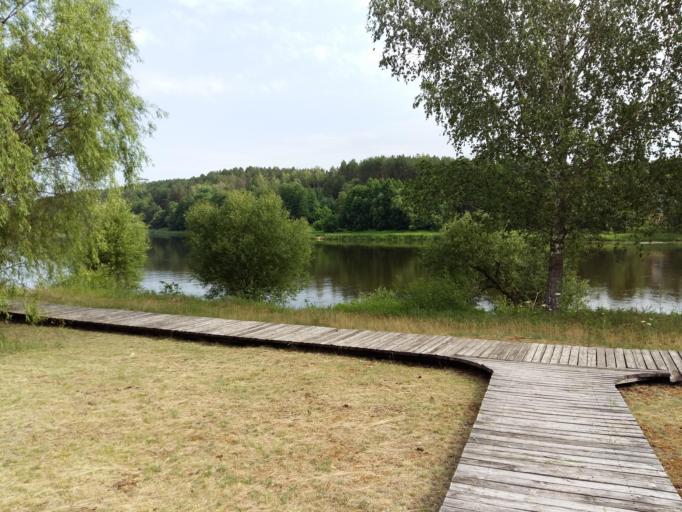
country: LT
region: Alytaus apskritis
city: Druskininkai
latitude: 54.1575
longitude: 24.1771
